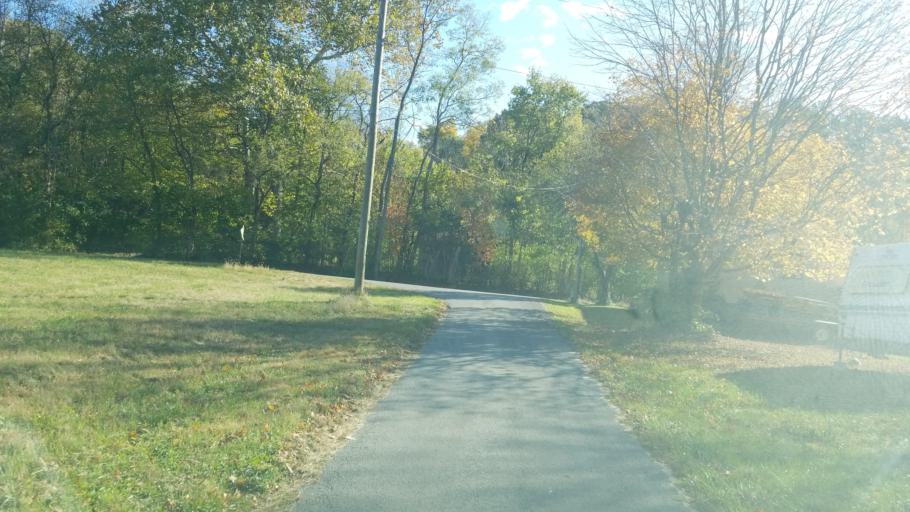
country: US
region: Ohio
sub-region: Warren County
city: Morrow
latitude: 39.3858
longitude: -84.0904
